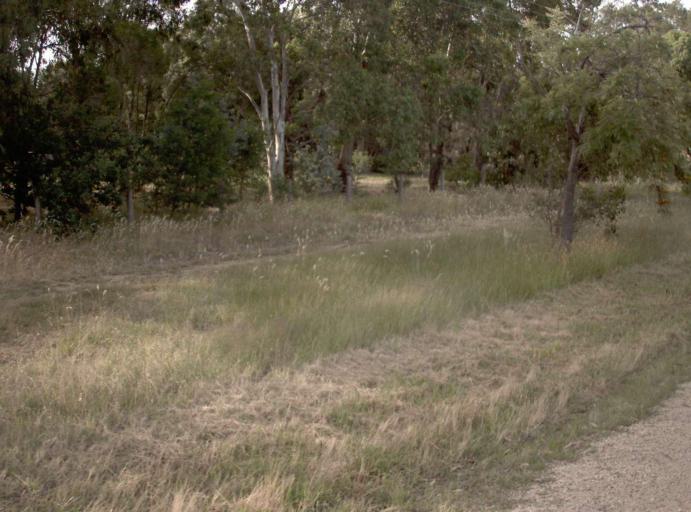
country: AU
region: Victoria
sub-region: Wellington
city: Sale
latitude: -37.9455
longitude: 146.9890
